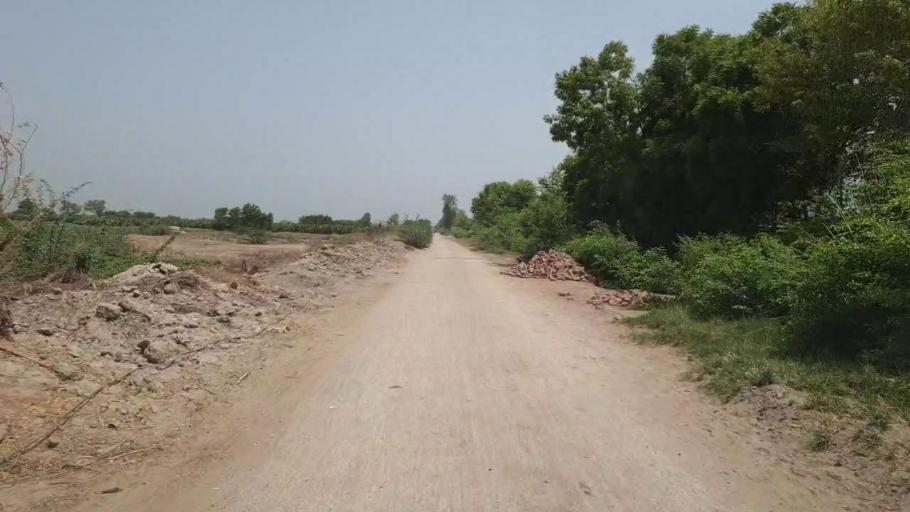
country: PK
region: Sindh
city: Nawabshah
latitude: 26.3032
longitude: 68.3041
